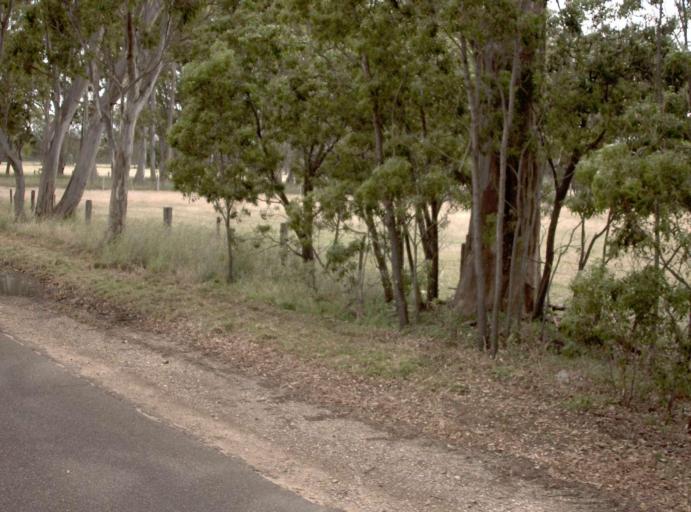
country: AU
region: Victoria
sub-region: Wellington
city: Sale
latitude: -37.8702
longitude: 147.0674
